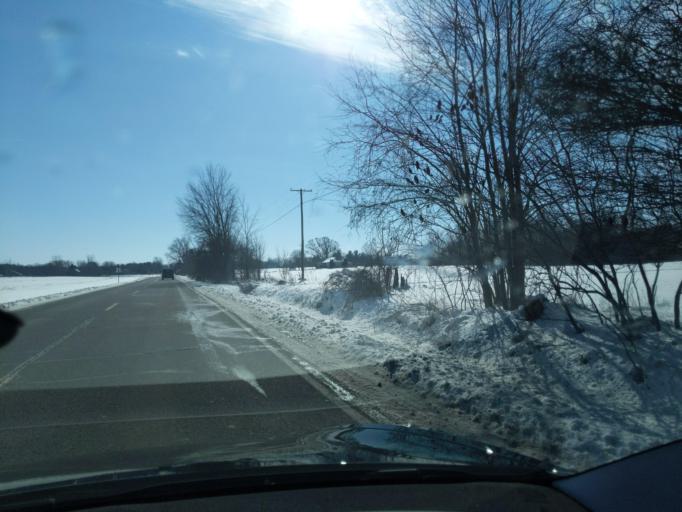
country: US
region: Michigan
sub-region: Livingston County
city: Fowlerville
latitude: 42.6401
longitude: -84.0723
